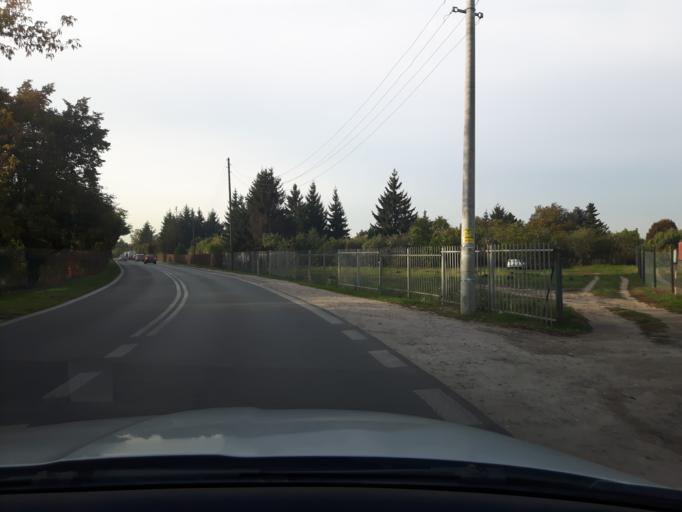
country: PL
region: Masovian Voivodeship
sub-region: Powiat wolominski
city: Zabki
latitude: 52.2836
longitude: 21.0967
